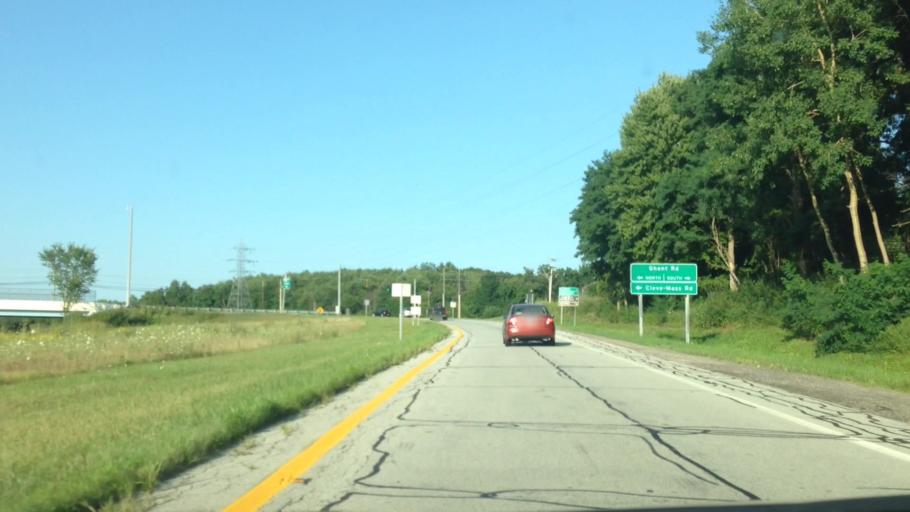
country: US
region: Ohio
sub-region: Summit County
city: Montrose-Ghent
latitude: 41.1493
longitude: -81.6318
